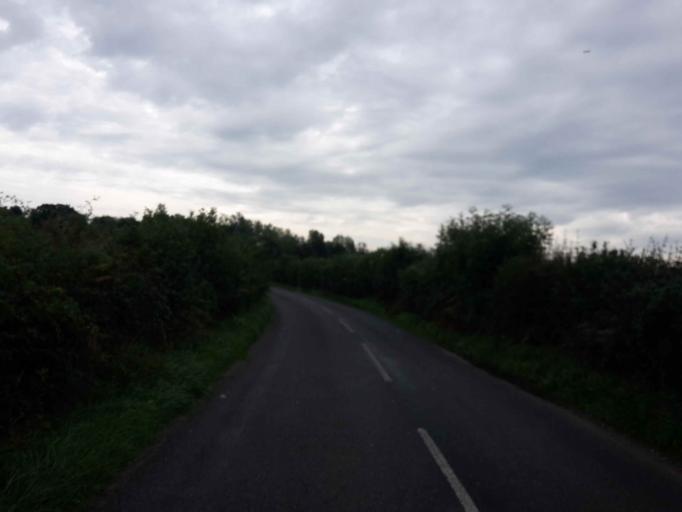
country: GB
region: England
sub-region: West Sussex
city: Rudgwick
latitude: 51.0707
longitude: -0.4506
